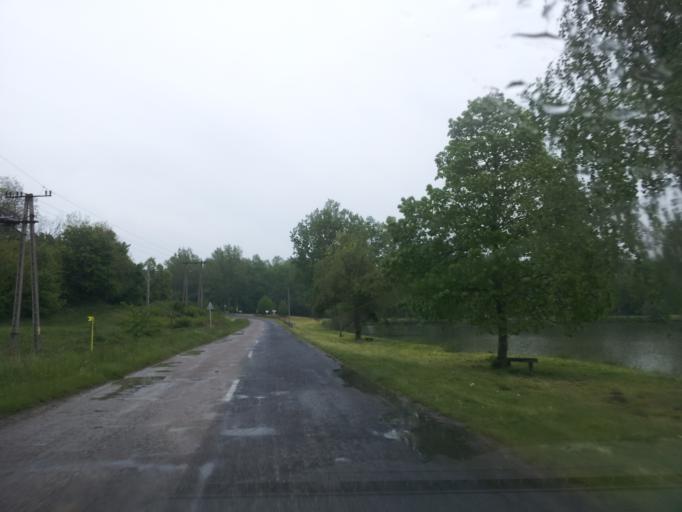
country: HU
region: Tolna
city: Szentgalpuszta
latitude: 46.2738
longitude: 18.6323
